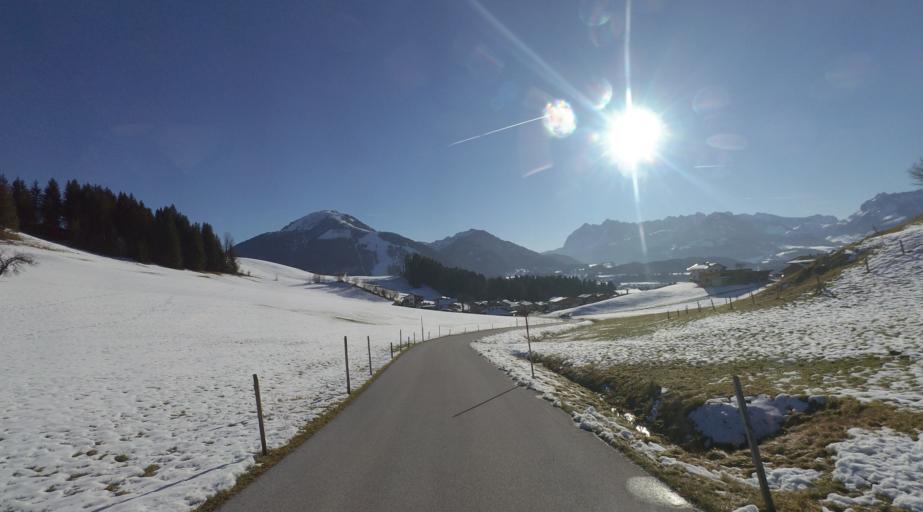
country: AT
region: Tyrol
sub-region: Politischer Bezirk Kitzbuhel
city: Kossen
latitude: 47.6740
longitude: 12.4164
